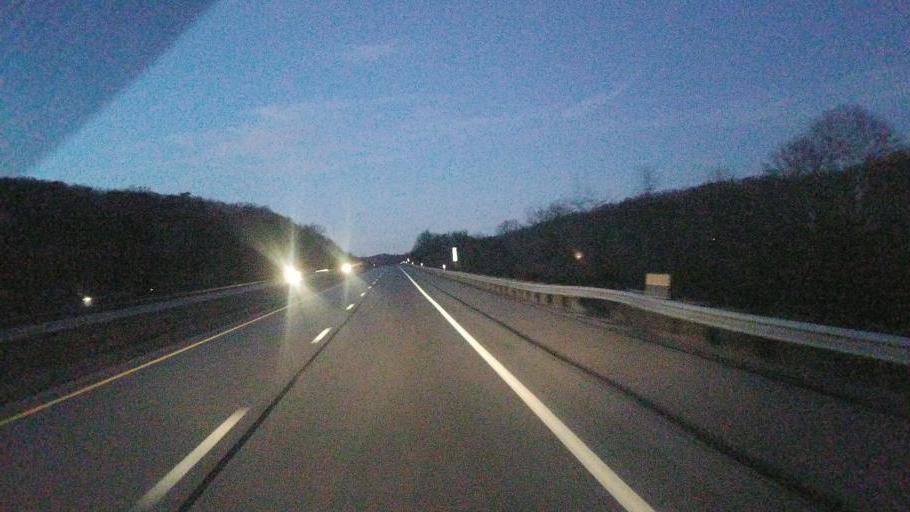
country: US
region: West Virginia
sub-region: Wood County
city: Mineral Wells
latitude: 39.1194
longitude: -81.5459
